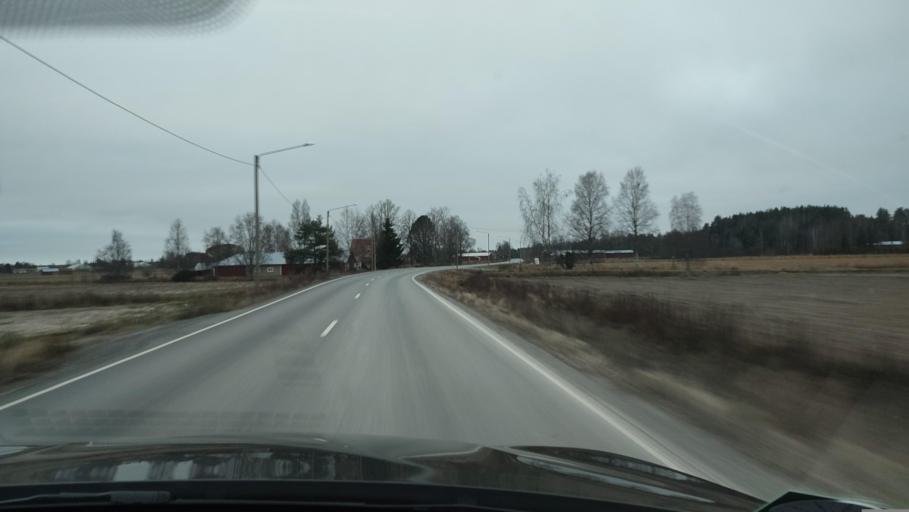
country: FI
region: Southern Ostrobothnia
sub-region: Suupohja
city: Karijoki
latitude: 62.2690
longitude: 21.5577
